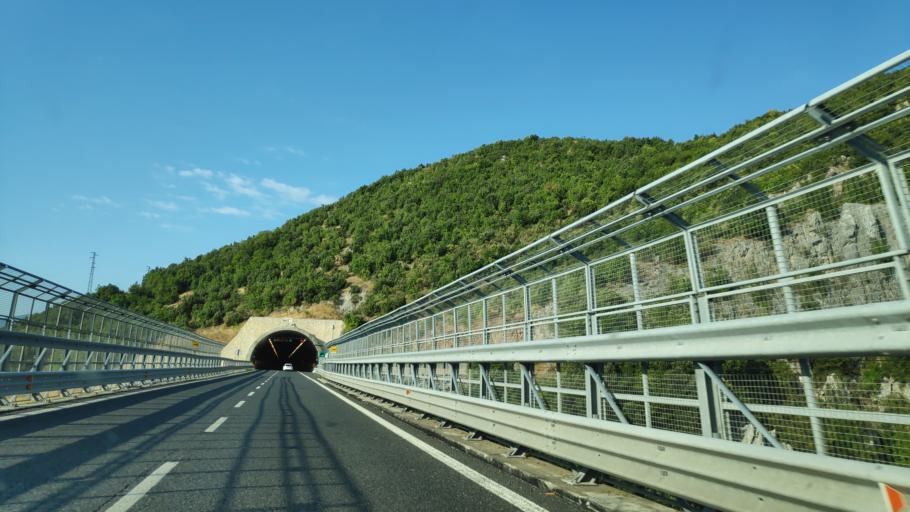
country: IT
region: Calabria
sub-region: Provincia di Cosenza
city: Morano Calabro
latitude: 39.8781
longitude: 16.1277
